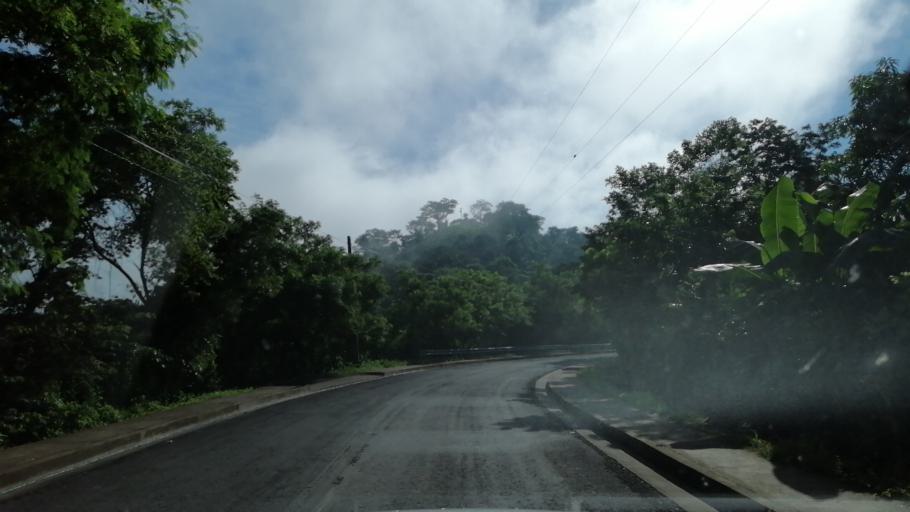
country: SV
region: Morazan
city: Cacaopera
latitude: 13.7742
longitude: -88.0871
